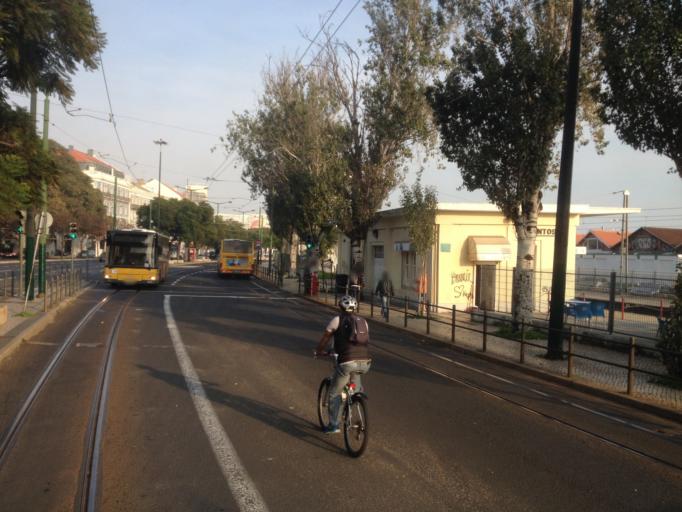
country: PT
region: Setubal
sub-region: Almada
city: Cacilhas
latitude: 38.7063
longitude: -9.1556
